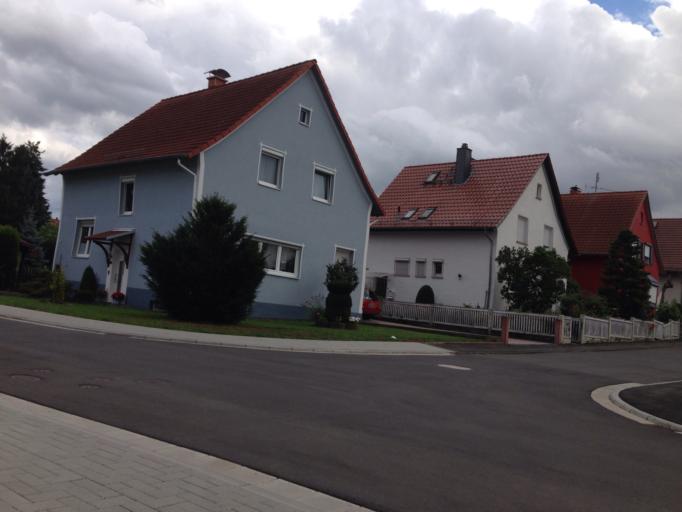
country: DE
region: Hesse
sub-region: Regierungsbezirk Giessen
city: Hungen
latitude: 50.4740
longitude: 8.9054
